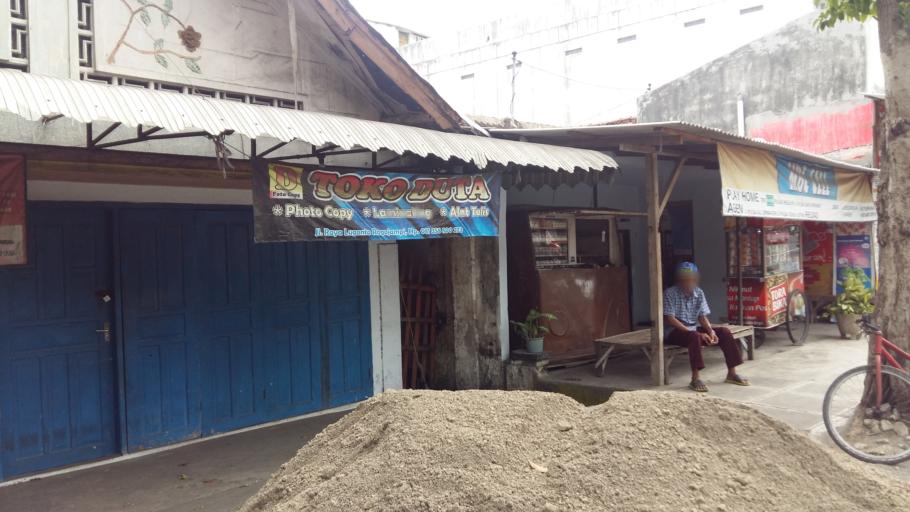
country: ID
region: East Java
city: Krajan
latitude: -8.3107
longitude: 114.2917
